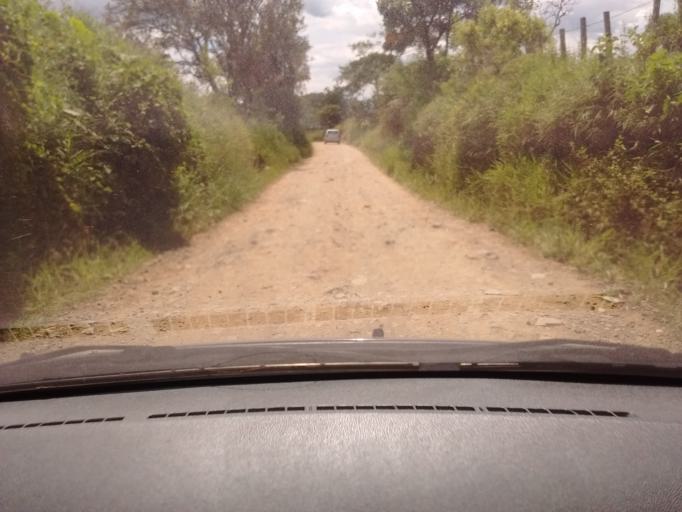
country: CO
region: Cauca
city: El Tambo
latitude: 2.4491
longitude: -76.8230
